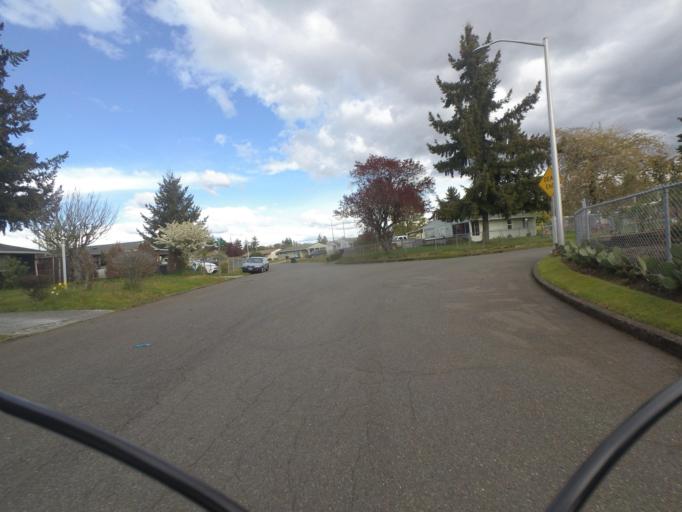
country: US
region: Washington
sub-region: Pierce County
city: Lakewood
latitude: 47.1653
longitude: -122.4971
